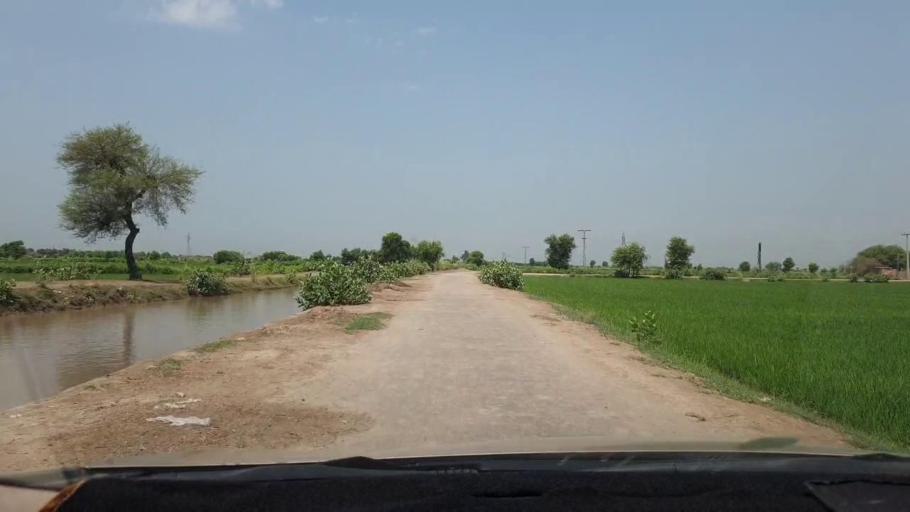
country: PK
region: Sindh
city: Naudero
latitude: 27.6603
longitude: 68.3250
